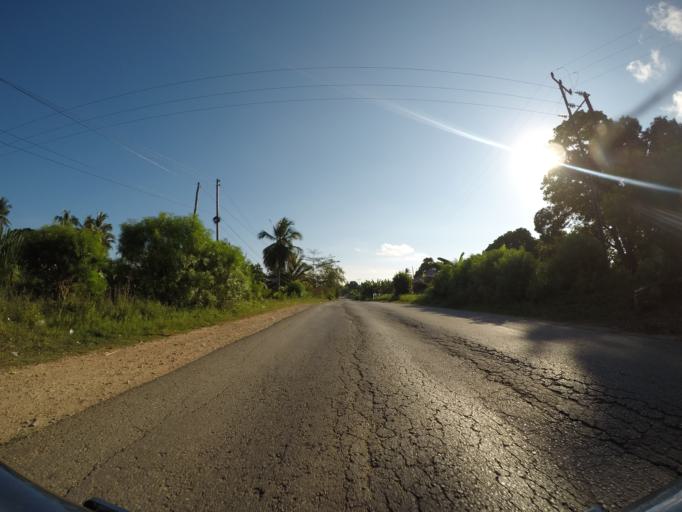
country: TZ
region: Pemba South
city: Chake Chake
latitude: -5.2884
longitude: 39.7622
